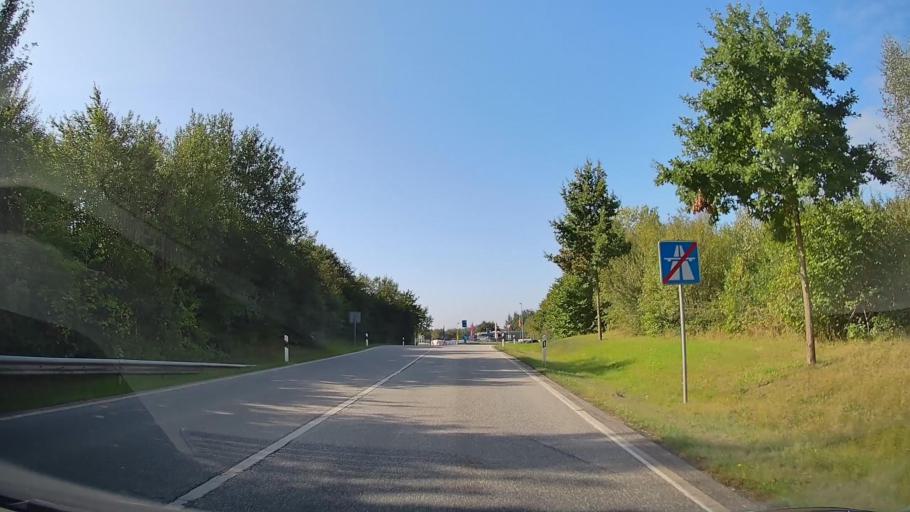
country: DE
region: Schleswig-Holstein
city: Oldenburg in Holstein
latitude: 54.3003
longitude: 10.8887
